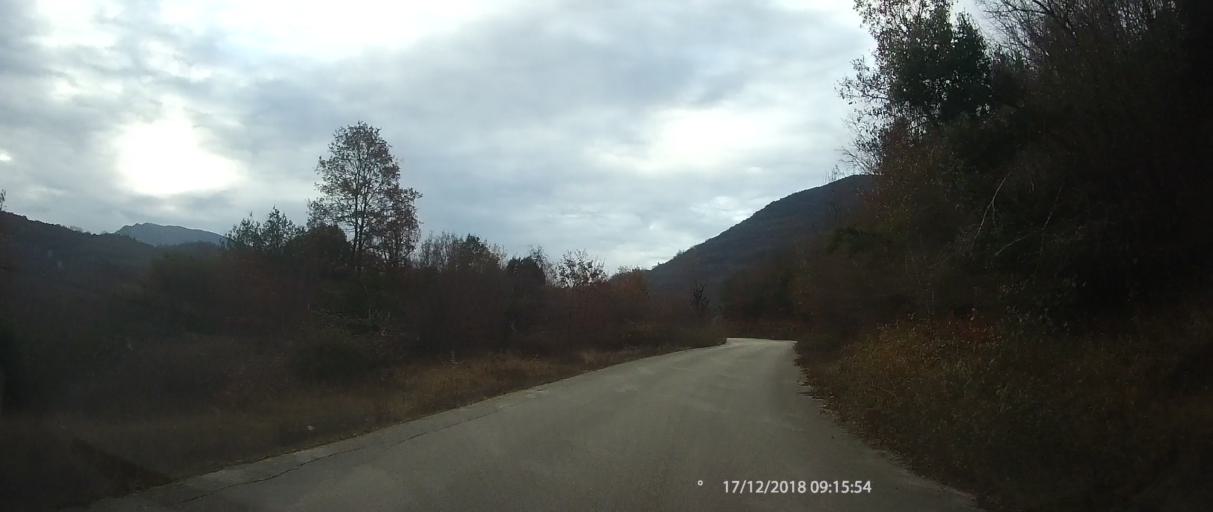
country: GR
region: Epirus
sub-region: Nomos Ioanninon
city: Kalpaki
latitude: 39.9649
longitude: 20.6567
